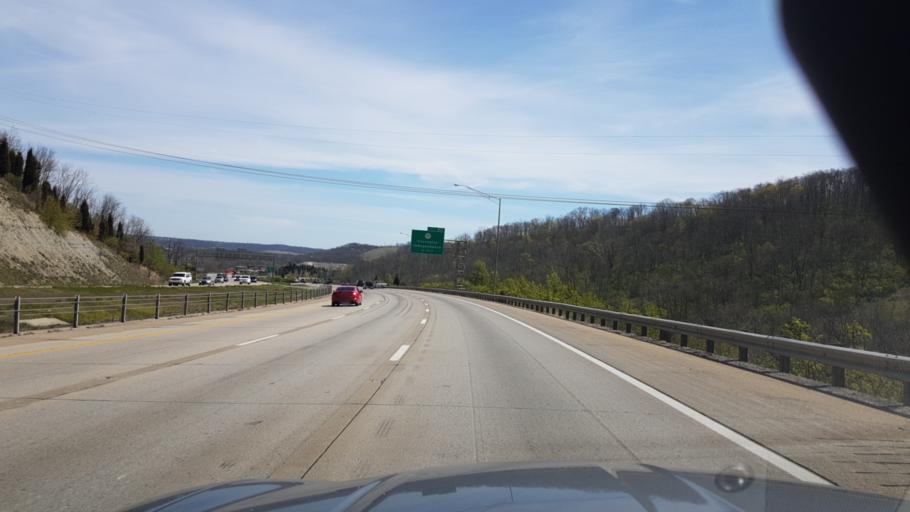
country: US
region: Kentucky
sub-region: Kenton County
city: Lakeside Park
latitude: 39.0263
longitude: -84.5478
